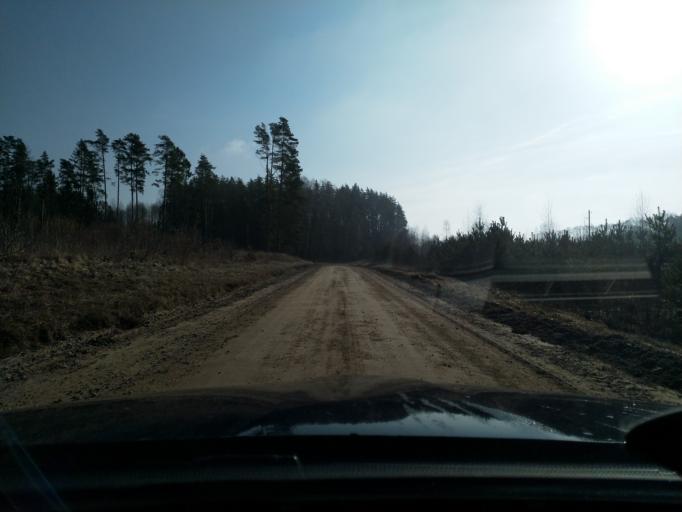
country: LV
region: Kuldigas Rajons
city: Kuldiga
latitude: 56.8684
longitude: 21.9216
